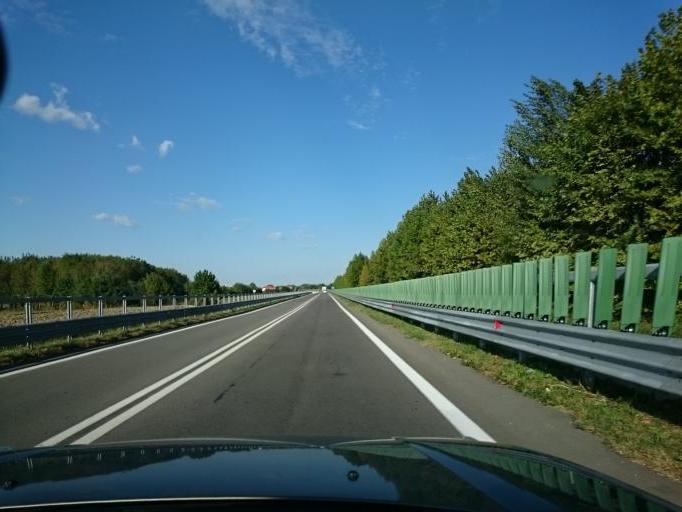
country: IT
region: Veneto
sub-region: Provincia di Padova
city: Tencarola
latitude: 45.3712
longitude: 11.8228
